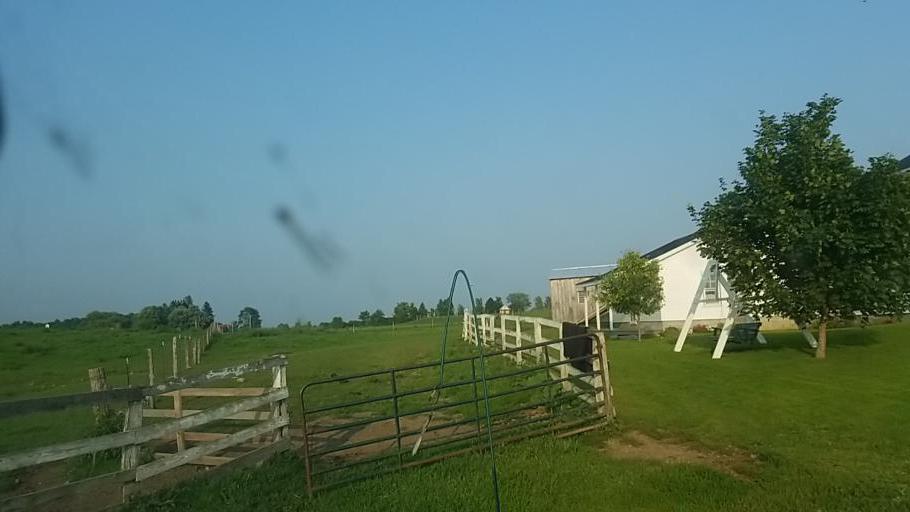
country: US
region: New York
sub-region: Montgomery County
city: Fonda
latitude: 42.9038
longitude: -74.4211
